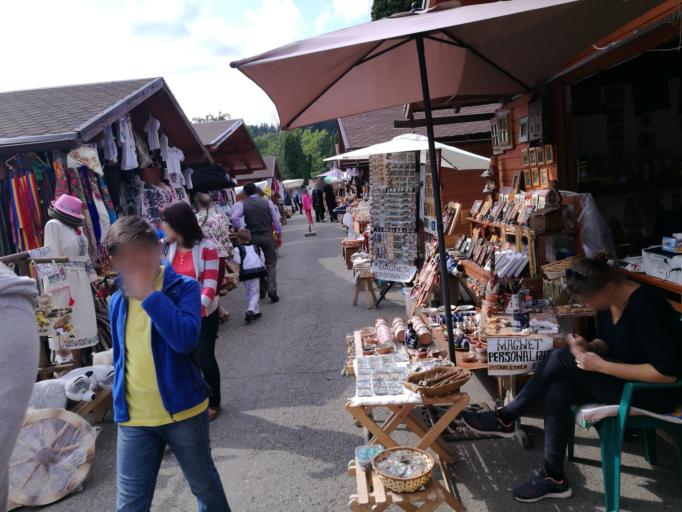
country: RO
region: Suceava
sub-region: Oras Gura Humorului
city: Gura Humorului
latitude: 47.5197
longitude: 25.8652
